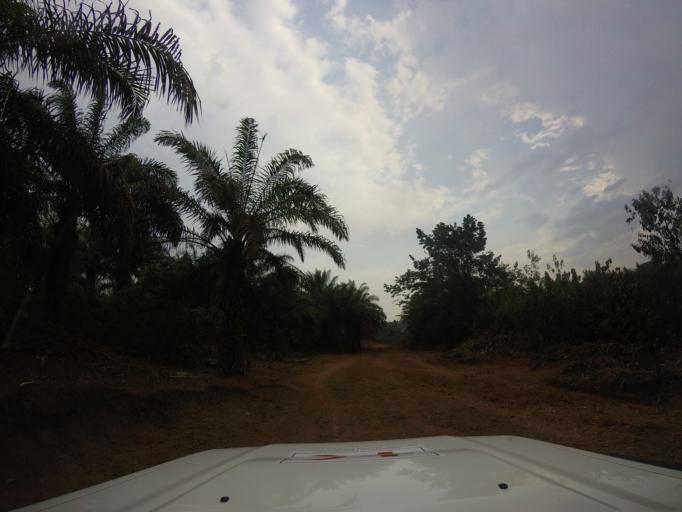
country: SL
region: Southern Province
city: Zimmi
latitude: 7.0825
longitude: -11.2700
